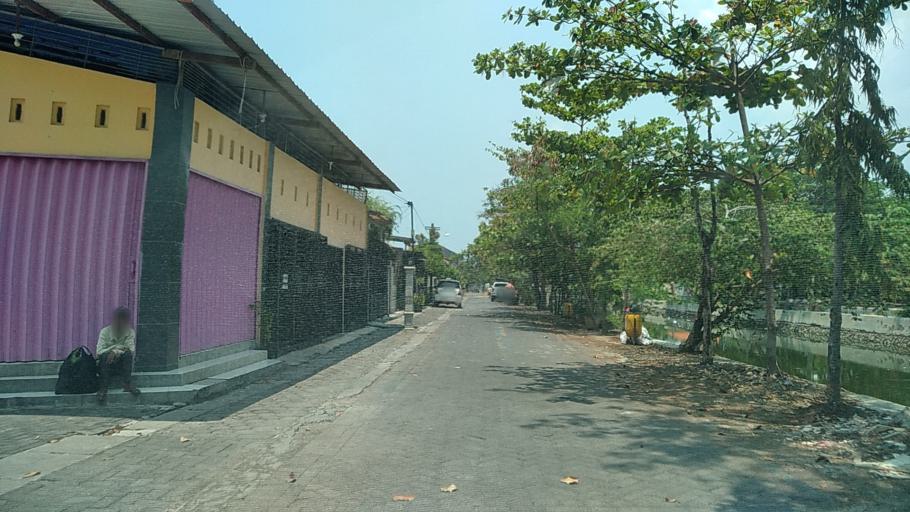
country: ID
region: Central Java
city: Semarang
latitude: -6.9735
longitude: 110.4376
